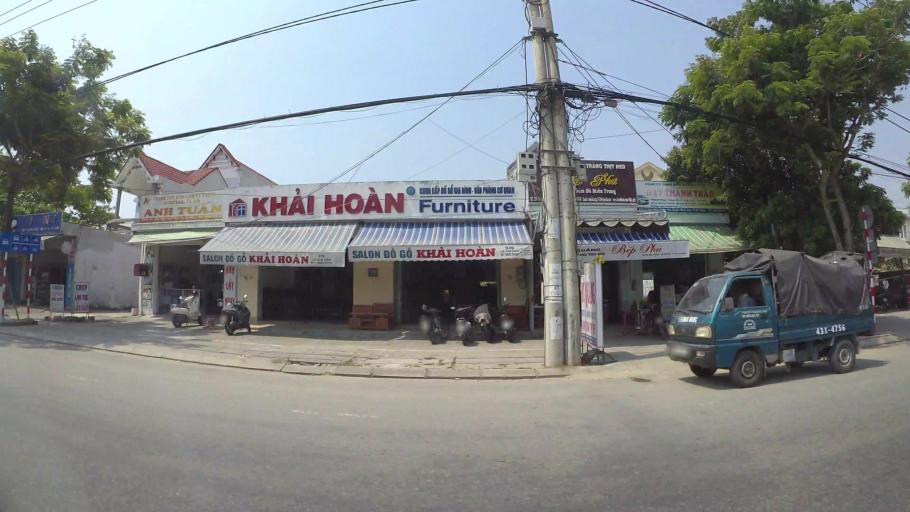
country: VN
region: Da Nang
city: Ngu Hanh Son
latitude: 16.0091
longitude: 108.2576
